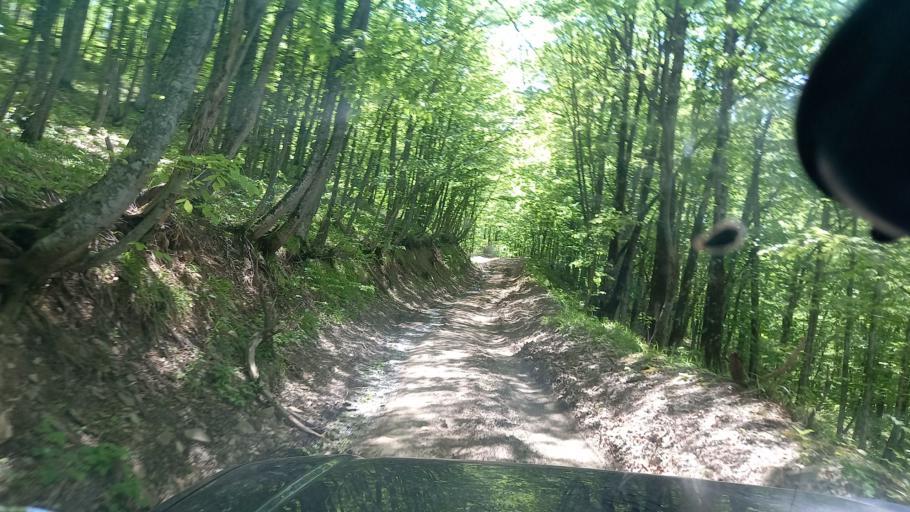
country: RU
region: Krasnodarskiy
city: Tuapse
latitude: 44.2559
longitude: 39.2840
